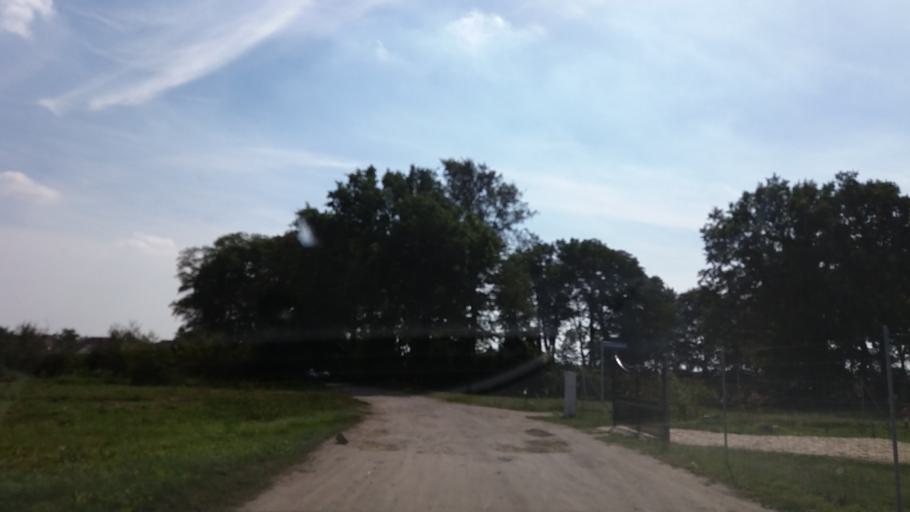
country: PL
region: West Pomeranian Voivodeship
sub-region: Powiat stargardzki
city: Stargard Szczecinski
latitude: 53.3696
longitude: 14.9687
